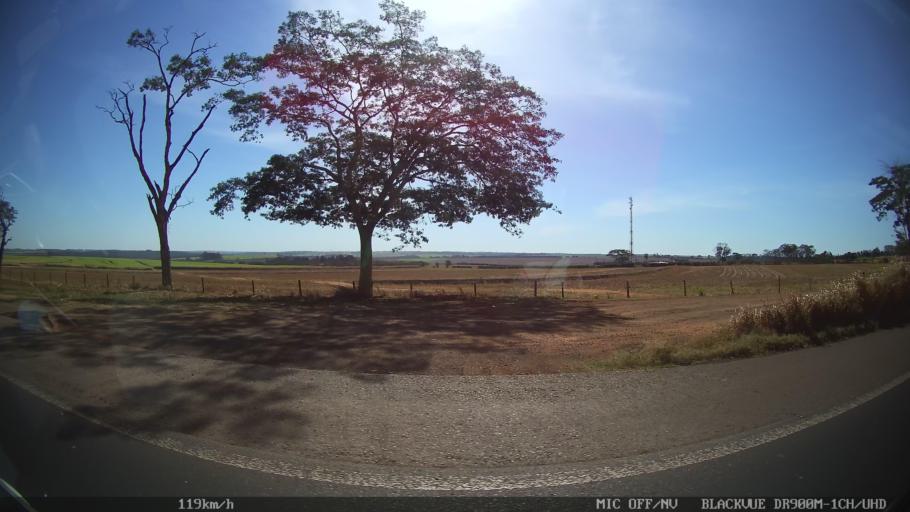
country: BR
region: Sao Paulo
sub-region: Barretos
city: Barretos
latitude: -20.5778
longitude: -48.6840
